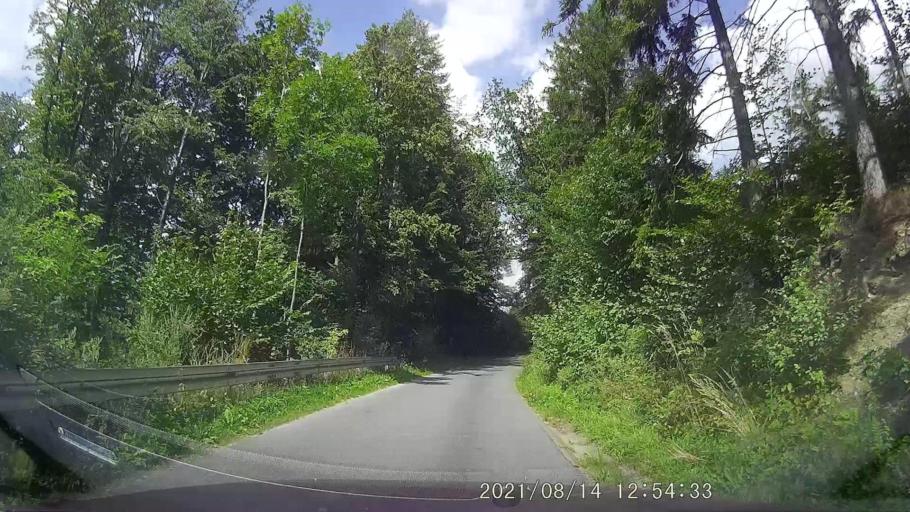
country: PL
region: Lower Silesian Voivodeship
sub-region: Powiat klodzki
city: Ladek-Zdroj
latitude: 50.3274
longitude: 16.8248
